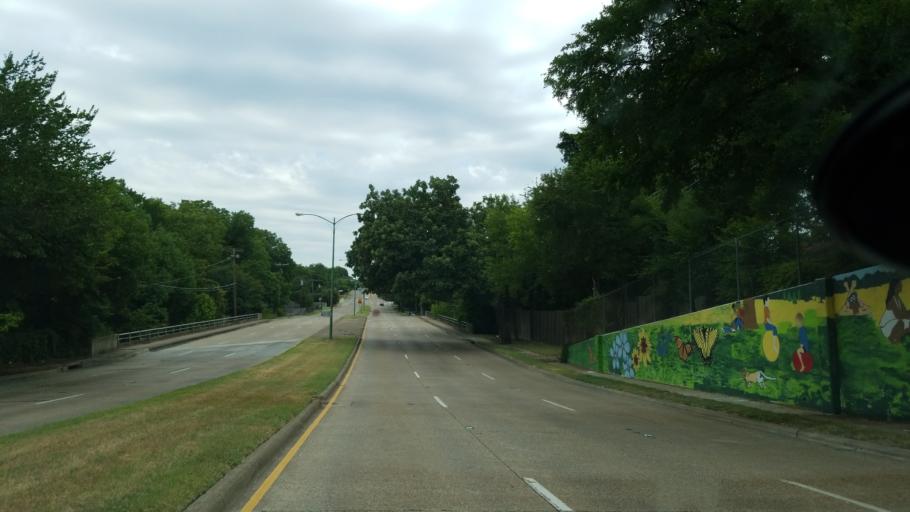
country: US
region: Texas
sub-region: Dallas County
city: Duncanville
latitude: 32.6695
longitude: -96.8401
